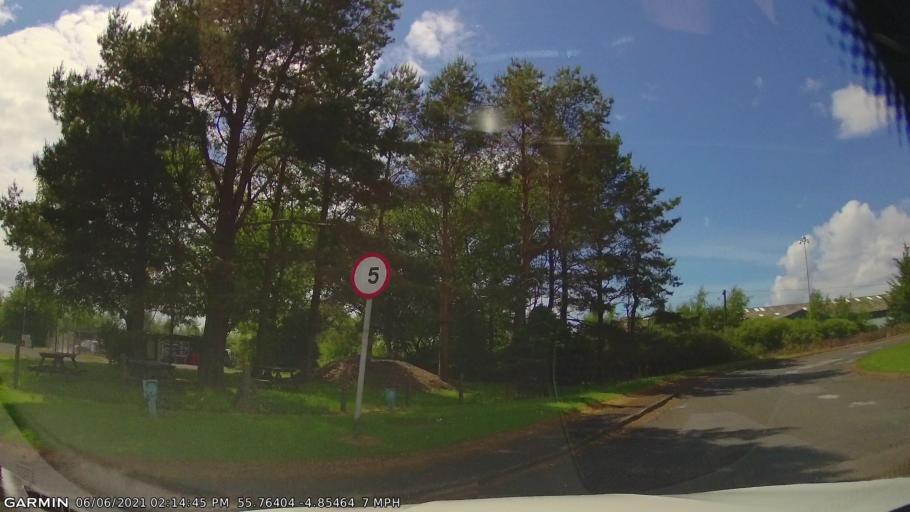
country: GB
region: Scotland
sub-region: North Ayrshire
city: Fairlie
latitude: 55.7640
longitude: -4.8546
